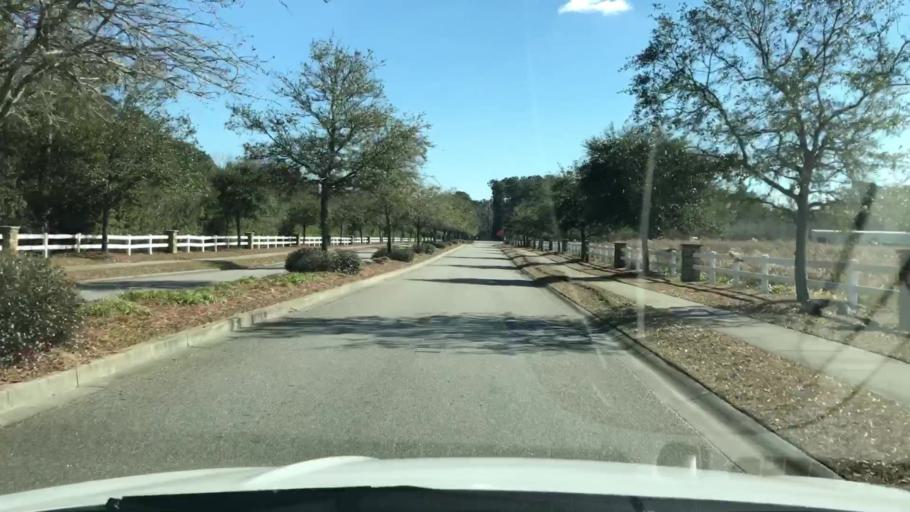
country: US
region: South Carolina
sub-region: Horry County
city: Socastee
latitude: 33.6418
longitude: -79.0333
